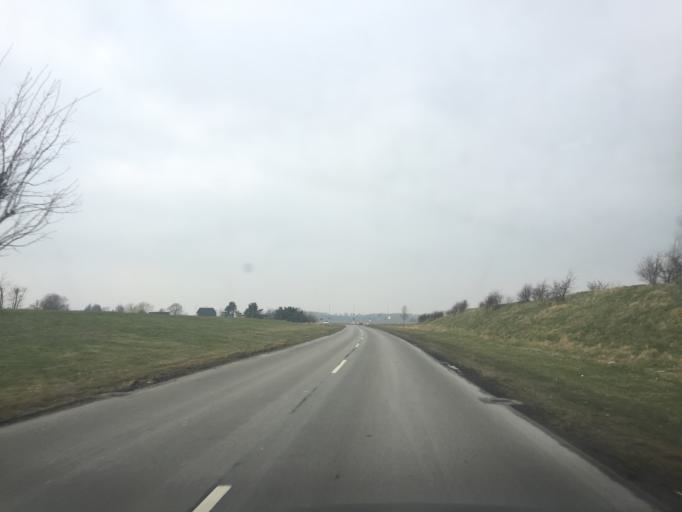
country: DK
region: Zealand
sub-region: Greve Kommune
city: Greve
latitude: 55.5971
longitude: 12.2590
